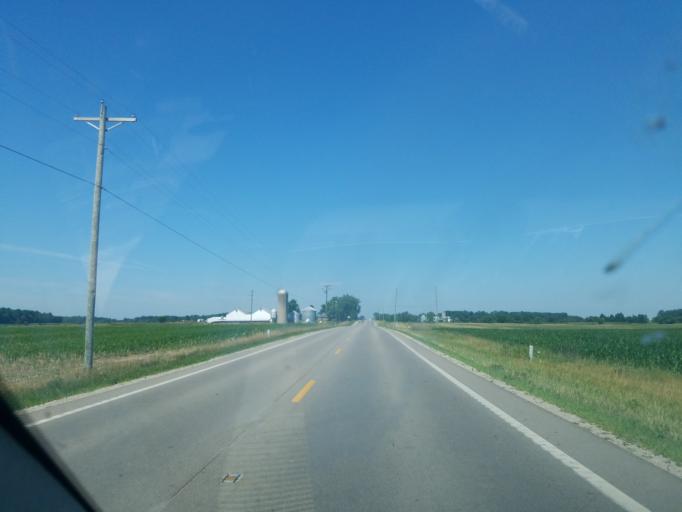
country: US
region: Ohio
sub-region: Shelby County
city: Botkins
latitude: 40.4388
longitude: -84.1433
